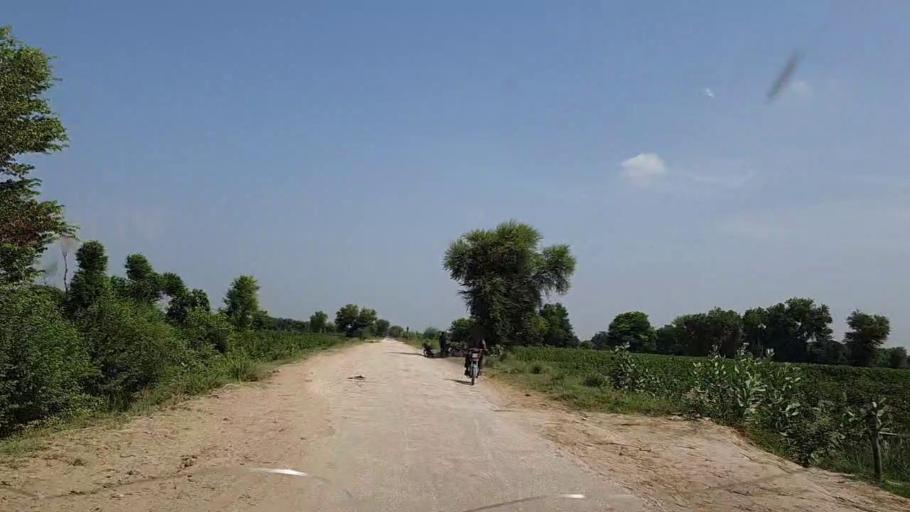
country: PK
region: Sindh
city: Adilpur
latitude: 27.8326
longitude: 69.2886
